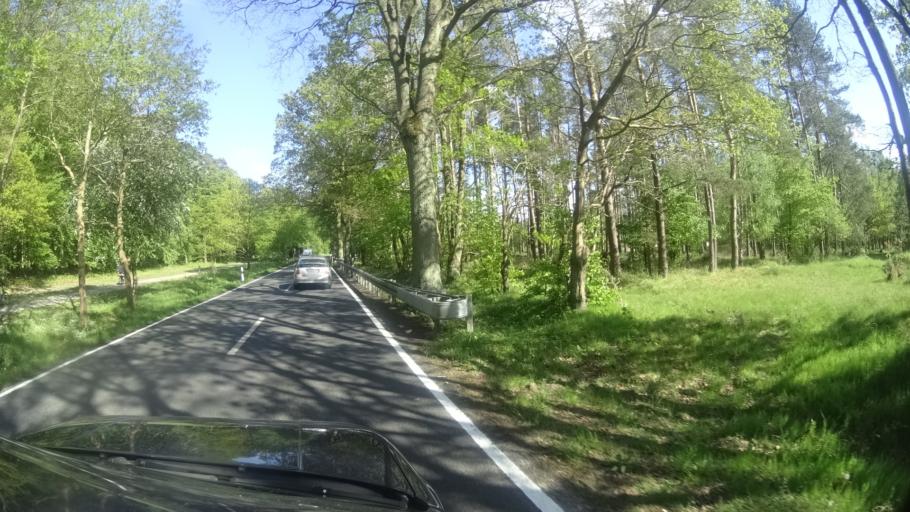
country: DE
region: Mecklenburg-Vorpommern
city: Gelbensande
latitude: 54.2546
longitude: 12.3049
